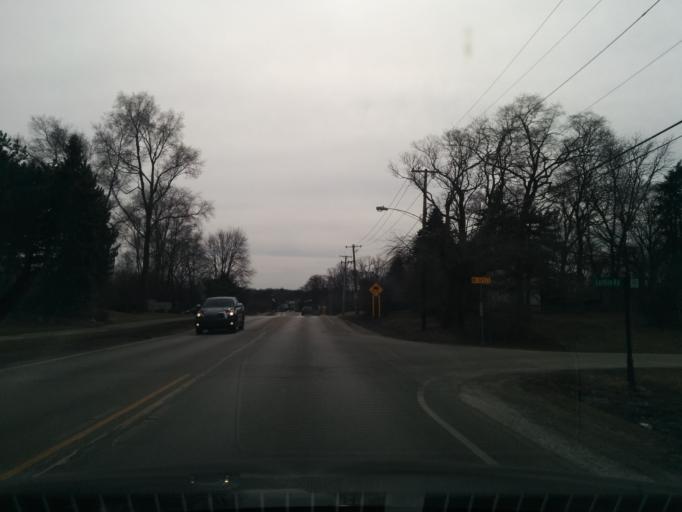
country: US
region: Illinois
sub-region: DuPage County
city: Oak Brook
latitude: 41.8228
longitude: -87.9263
